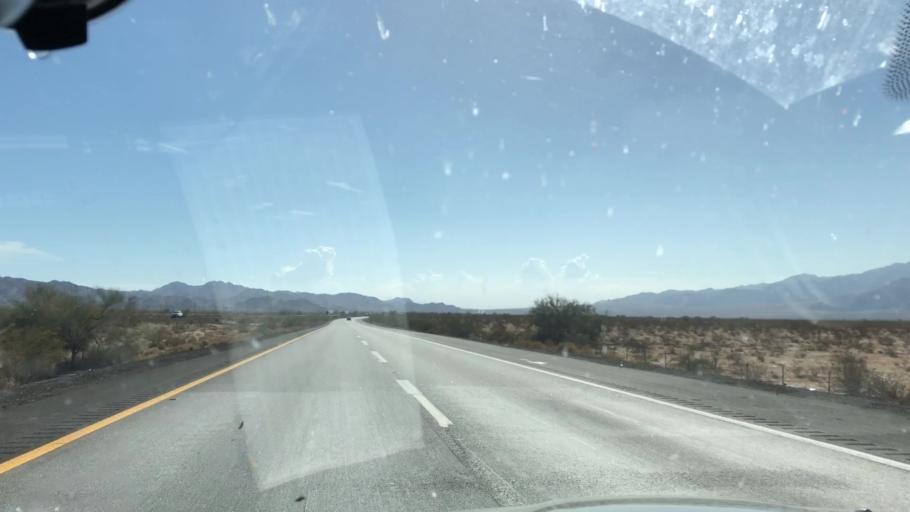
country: US
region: California
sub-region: Imperial County
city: Niland
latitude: 33.6754
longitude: -115.5754
